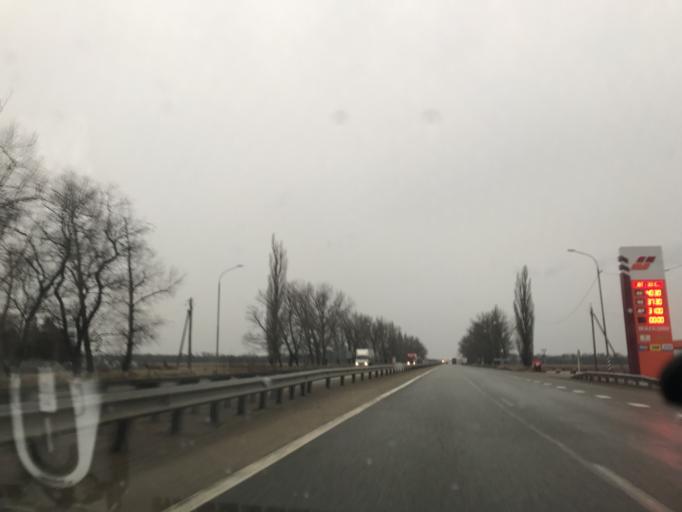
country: RU
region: Krasnodarskiy
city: Pavlovskaya
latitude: 46.2256
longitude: 39.8315
